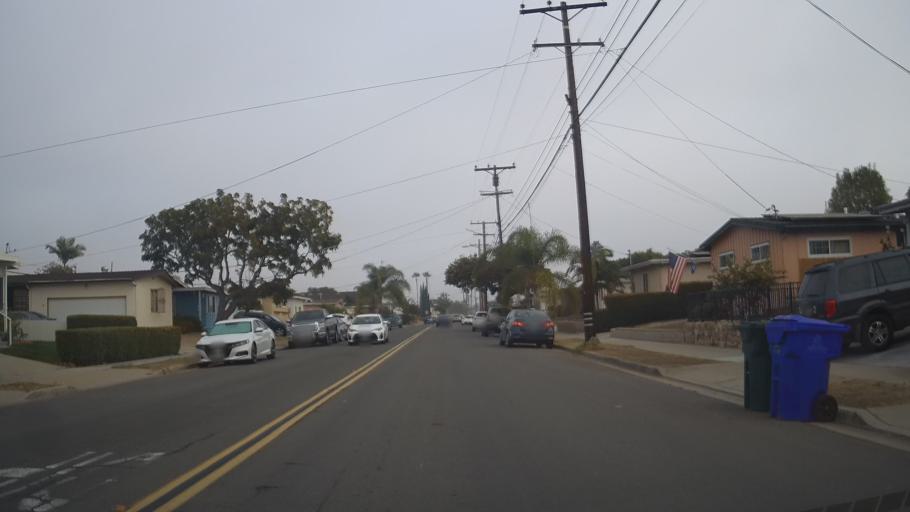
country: US
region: California
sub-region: San Diego County
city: San Diego
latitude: 32.7987
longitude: -117.1418
